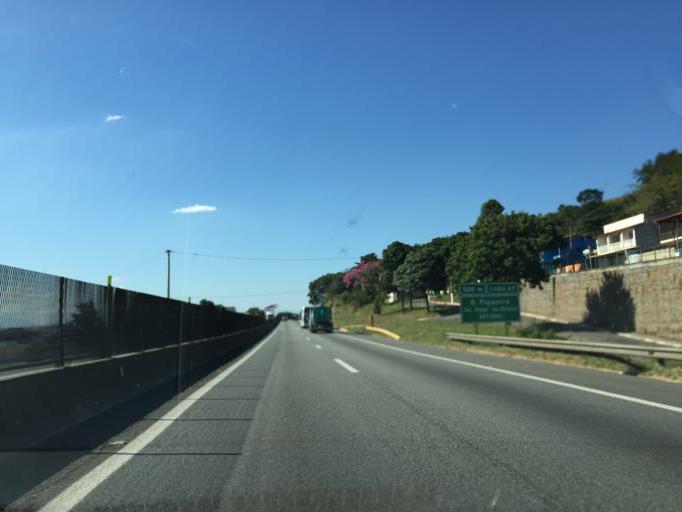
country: BR
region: Sao Paulo
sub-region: Aparecida
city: Aparecida
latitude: -22.8327
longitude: -45.2163
